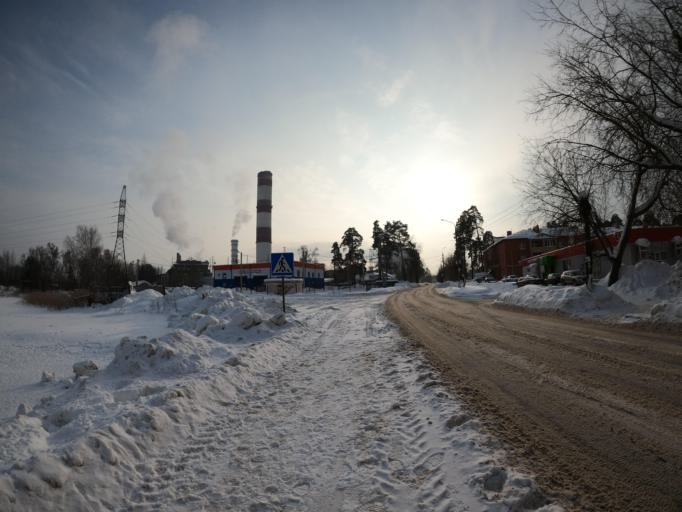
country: RU
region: Moskovskaya
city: Elektrogorsk
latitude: 55.8909
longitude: 38.7794
